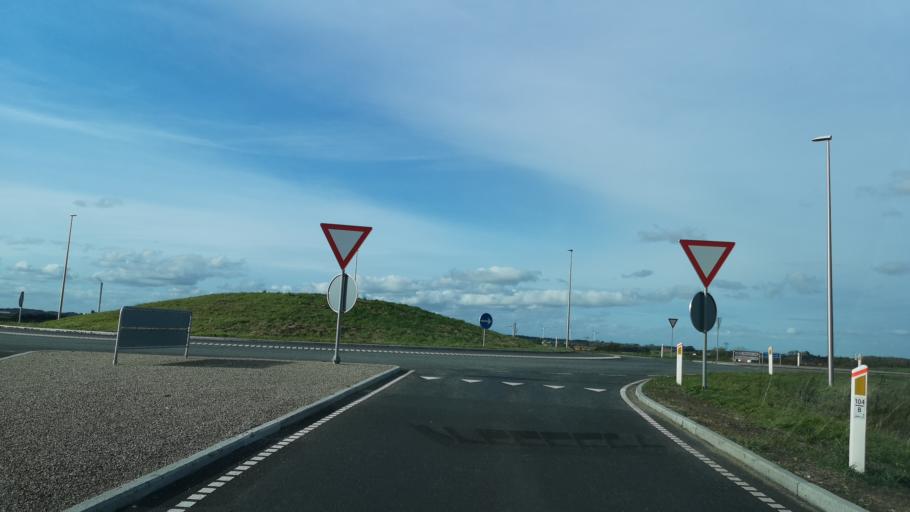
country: DK
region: Central Jutland
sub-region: Holstebro Kommune
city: Holstebro
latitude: 56.3869
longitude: 8.6557
